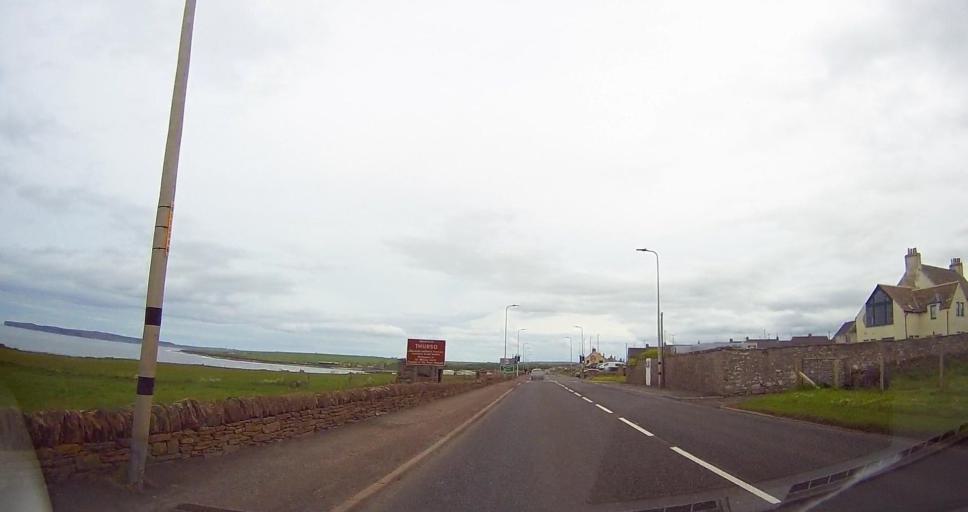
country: GB
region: Scotland
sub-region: Highland
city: Thurso
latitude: 58.5982
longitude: -3.5351
